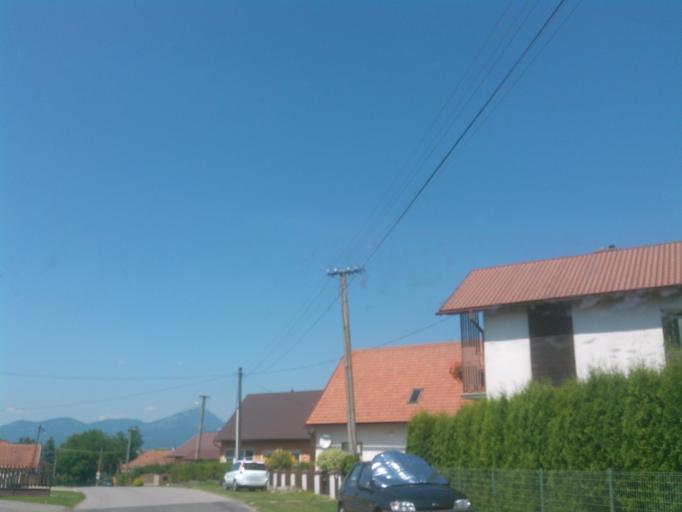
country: SK
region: Zilinsky
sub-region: Okres Liptovsky Mikulas
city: Liptovsky Mikulas
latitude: 49.0490
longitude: 19.4853
